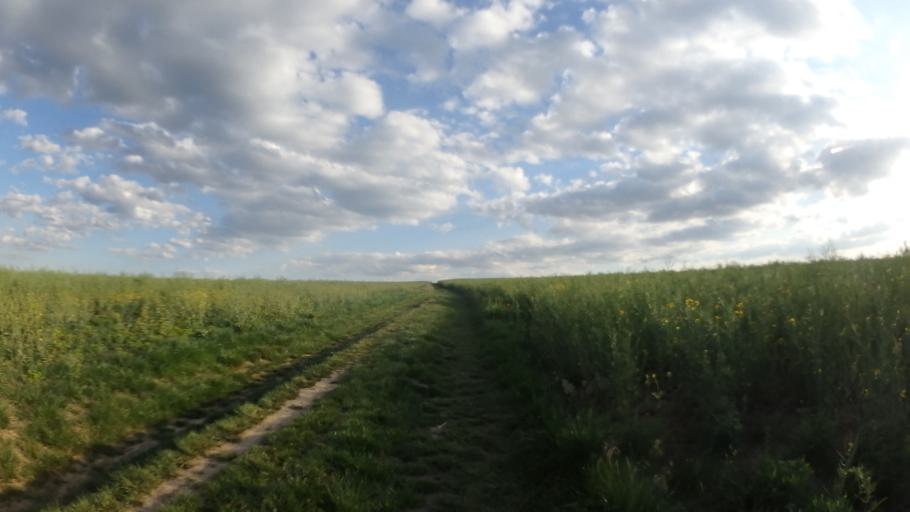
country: CZ
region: South Moravian
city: Moravany
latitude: 49.1418
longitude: 16.5930
